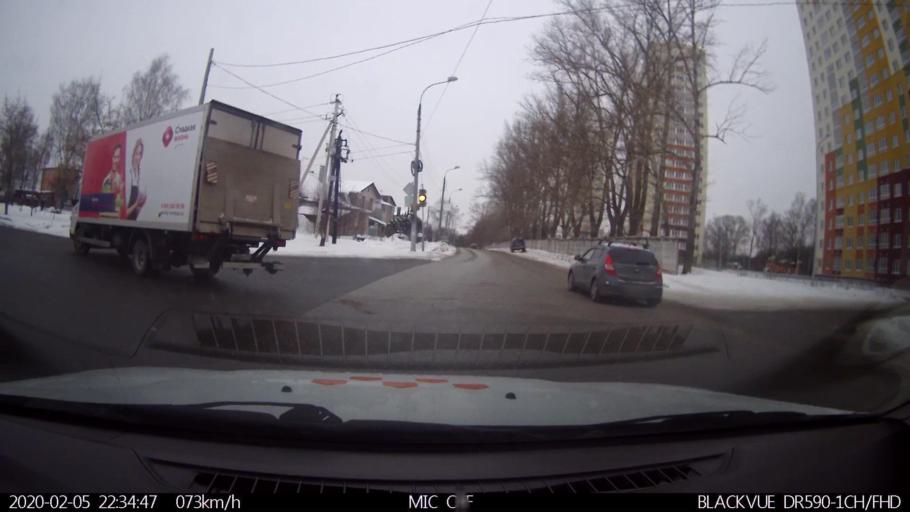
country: RU
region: Nizjnij Novgorod
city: Imeni Stepana Razina
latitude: 54.7347
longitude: 44.2294
